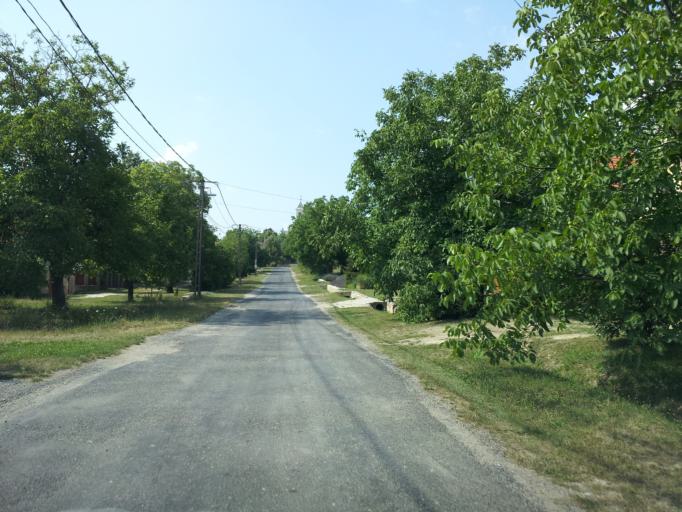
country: HU
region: Veszprem
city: Balatonfured
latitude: 47.0018
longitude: 17.8306
